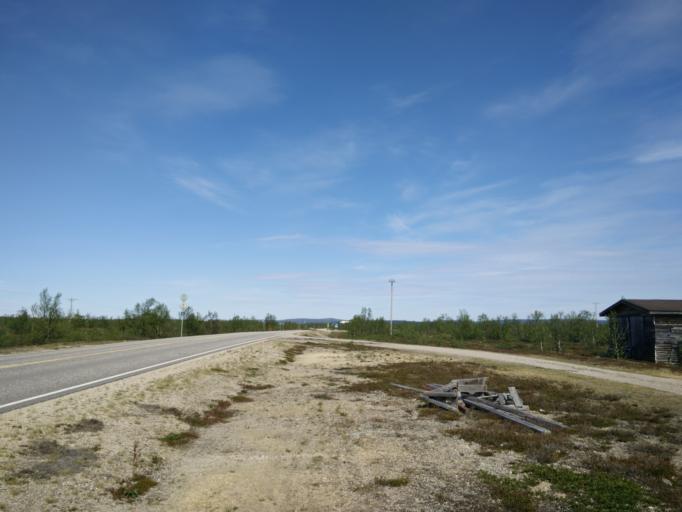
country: FI
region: Lapland
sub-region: Tunturi-Lappi
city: Enontekioe
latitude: 68.5620
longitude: 23.3276
